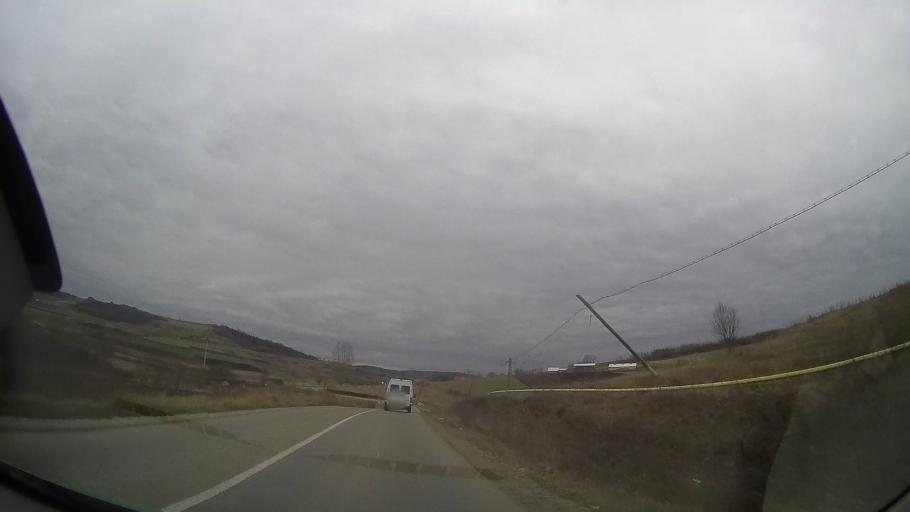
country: RO
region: Cluj
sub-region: Comuna Catina
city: Catina
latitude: 46.8015
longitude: 24.2139
